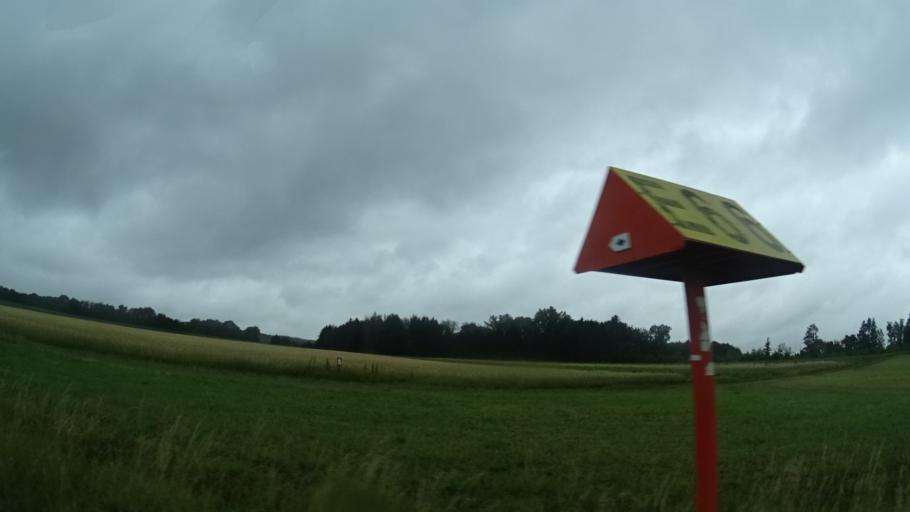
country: BE
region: Wallonia
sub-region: Province du Luxembourg
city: Messancy
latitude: 49.5933
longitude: 5.8385
